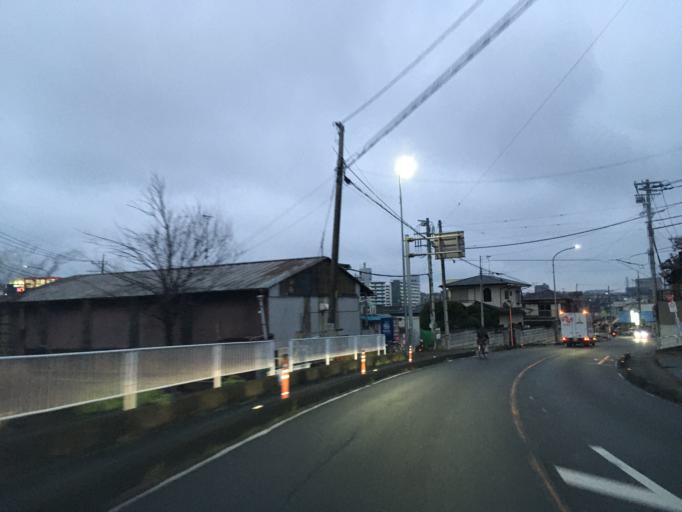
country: JP
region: Saitama
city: Asaka
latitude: 35.7903
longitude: 139.5850
